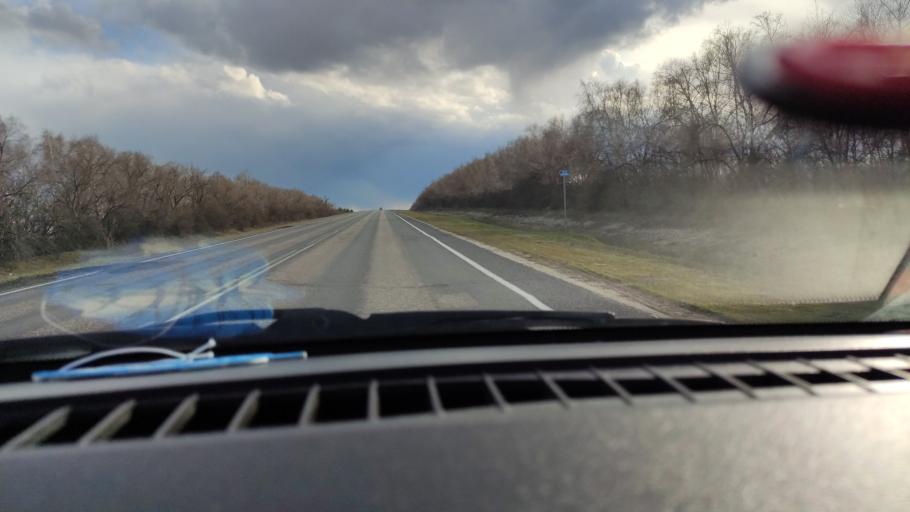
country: RU
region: Saratov
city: Sinodskoye
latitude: 51.9418
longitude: 46.5975
